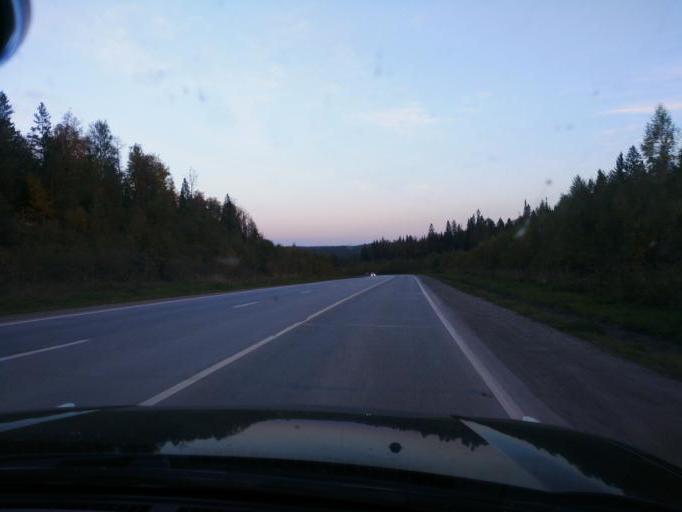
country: RU
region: Perm
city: Polazna
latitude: 58.2925
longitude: 56.4885
